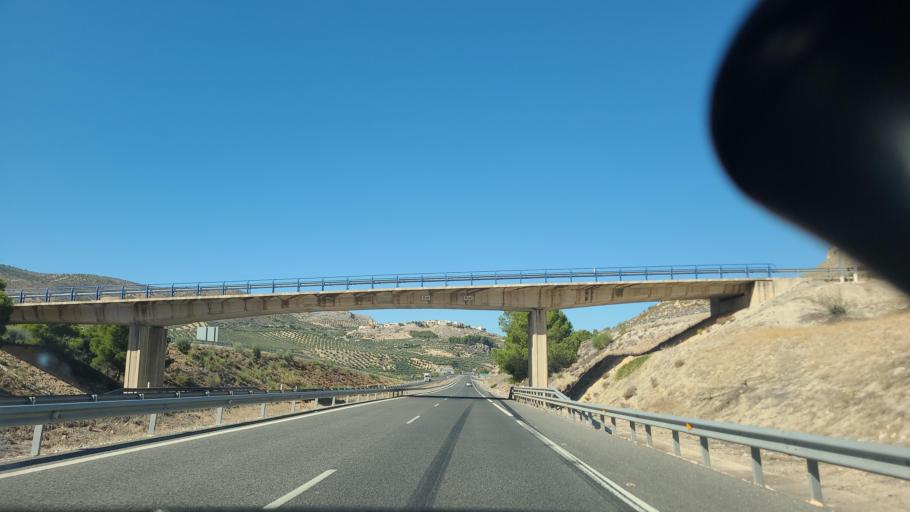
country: ES
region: Andalusia
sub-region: Provincia de Jaen
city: La Guardia de Jaen
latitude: 37.7246
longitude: -3.6789
